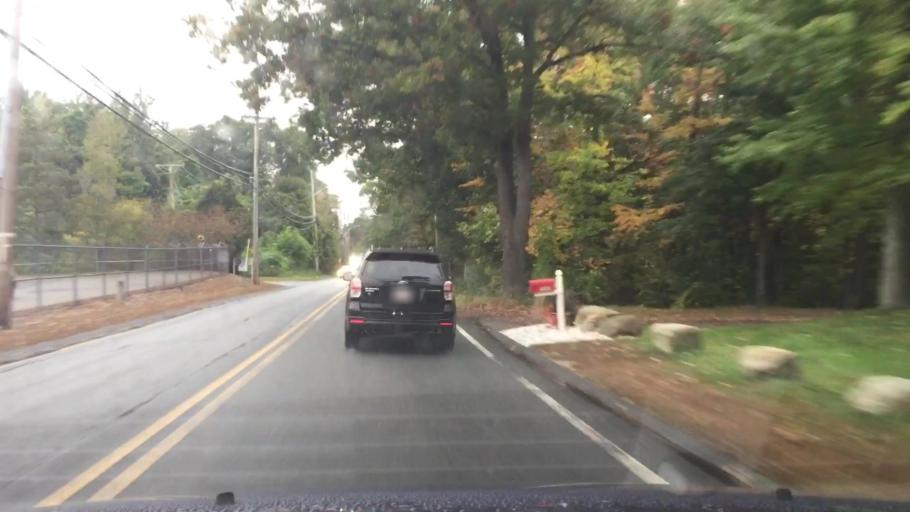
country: US
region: Massachusetts
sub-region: Middlesex County
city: Dracut
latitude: 42.6953
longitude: -71.2645
